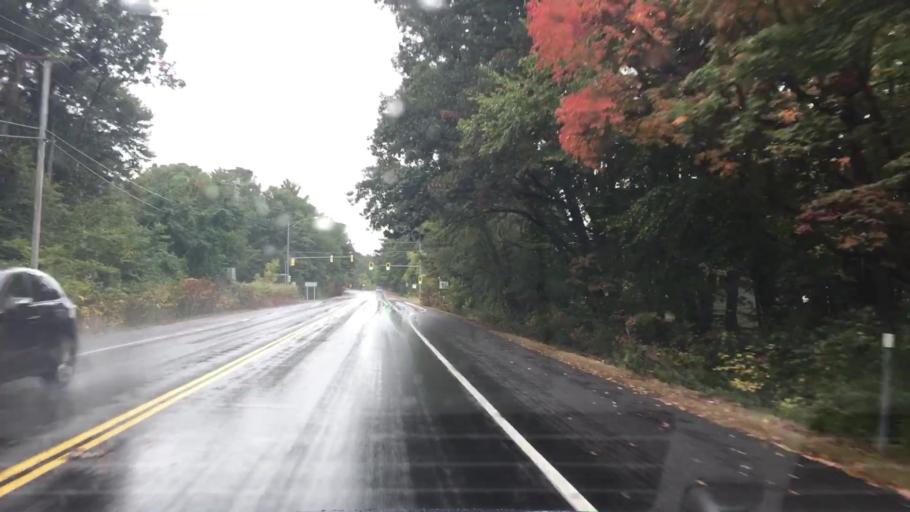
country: US
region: New Hampshire
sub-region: Rockingham County
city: Seabrook
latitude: 42.8710
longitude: -70.8539
